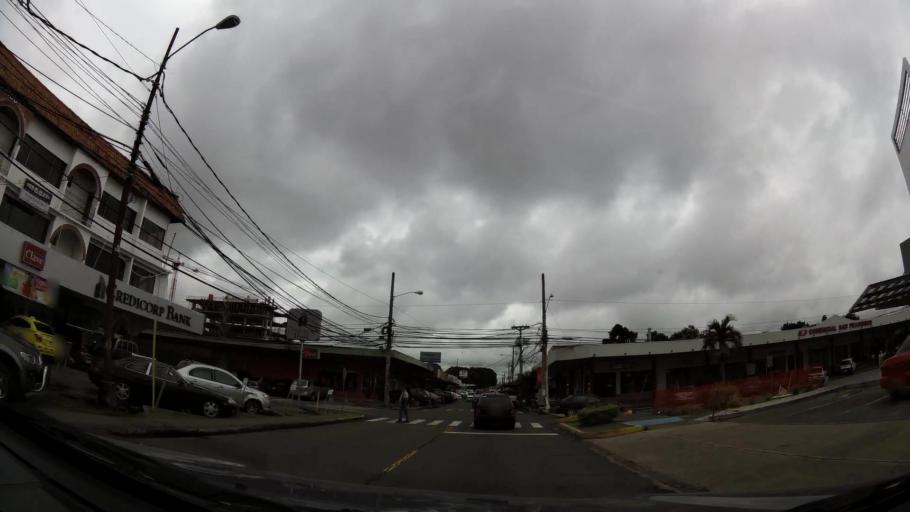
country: PA
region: Chiriqui
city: David
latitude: 8.4311
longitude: -82.4275
